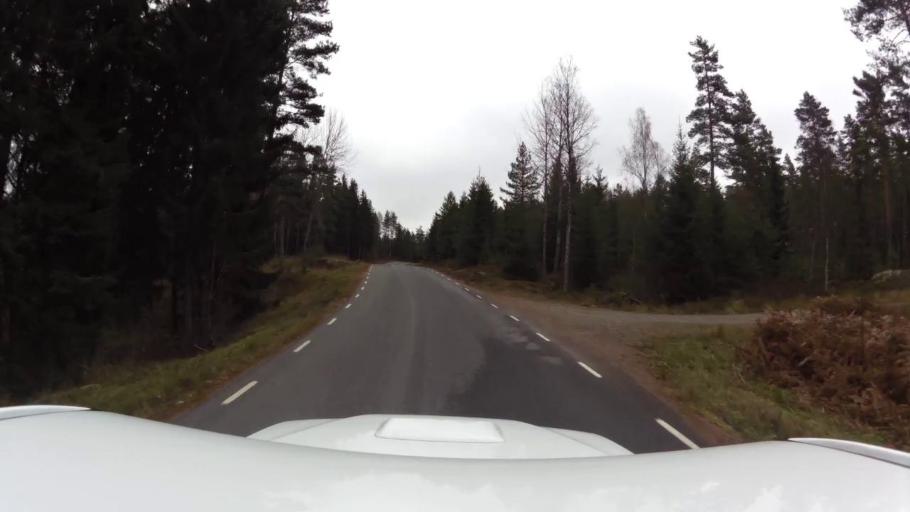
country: SE
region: OEstergoetland
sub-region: Kinda Kommun
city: Rimforsa
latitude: 58.1401
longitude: 15.4538
